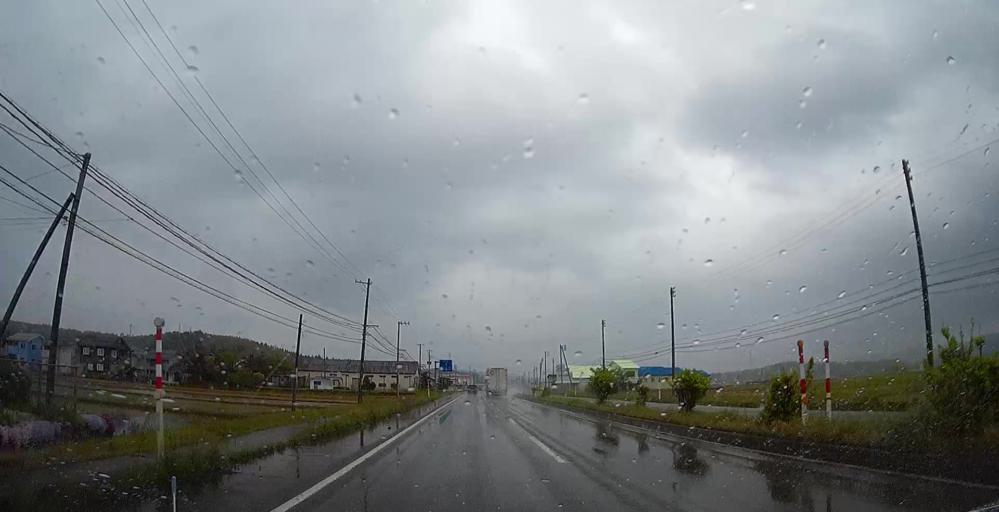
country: JP
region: Niigata
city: Kashiwazaki
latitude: 37.4282
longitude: 138.6220
